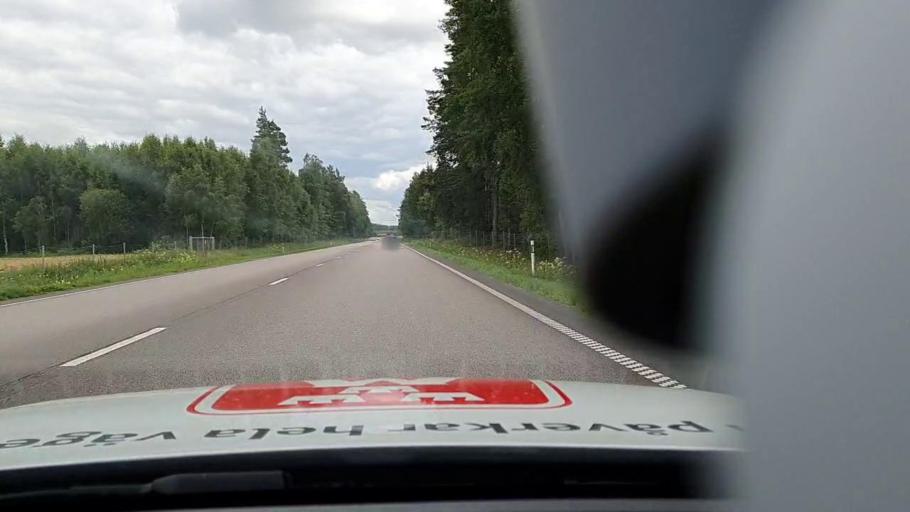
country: SE
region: Vaestra Goetaland
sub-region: Lidkopings Kommun
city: Vinninga
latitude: 58.4595
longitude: 13.2293
